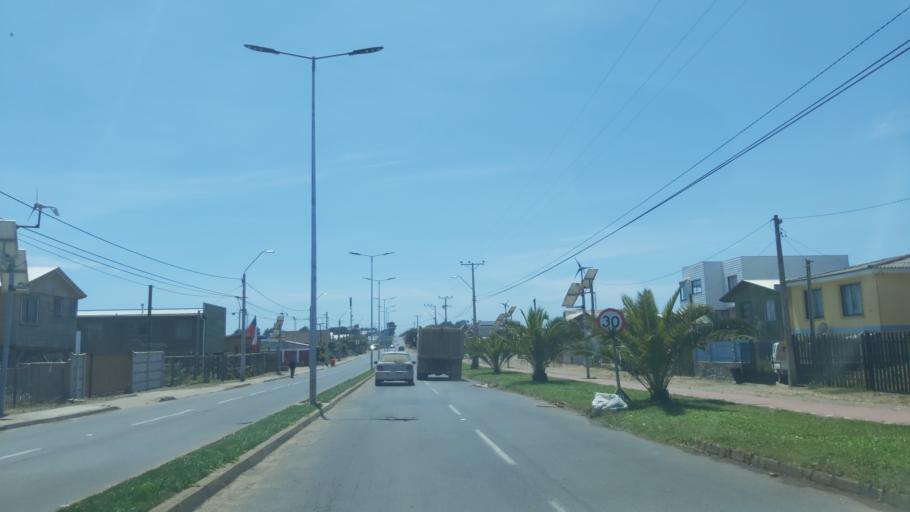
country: CL
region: Maule
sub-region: Provincia de Cauquenes
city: Cauquenes
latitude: -35.8101
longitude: -72.5713
